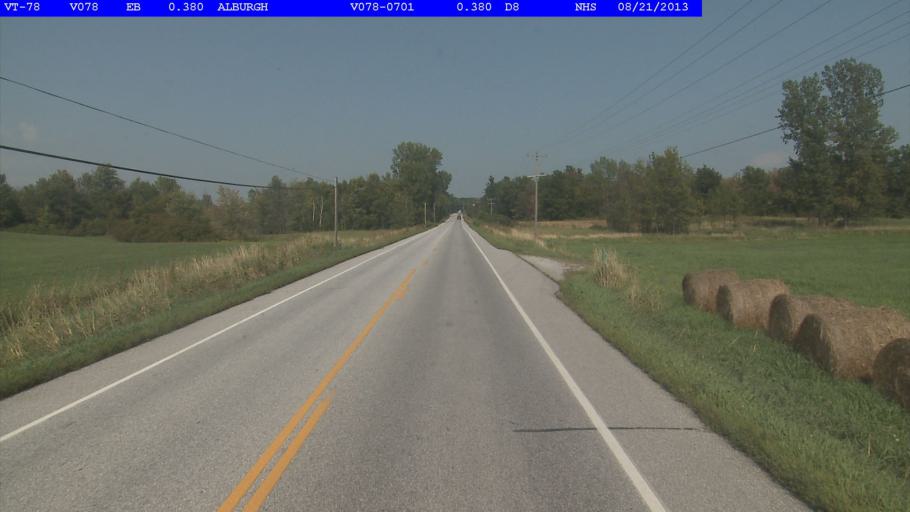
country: US
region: New York
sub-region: Clinton County
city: Rouses Point
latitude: 44.9644
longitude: -73.2727
